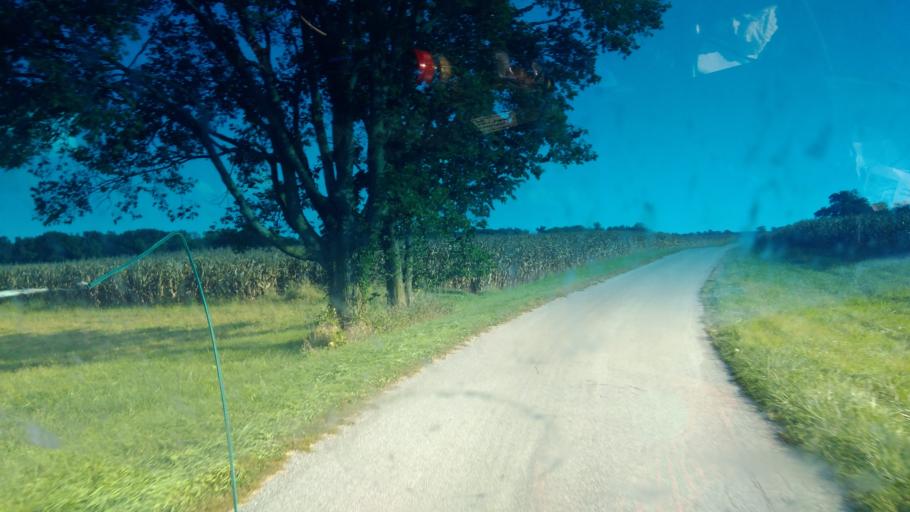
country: US
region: Ohio
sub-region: Wyandot County
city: Upper Sandusky
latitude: 40.8997
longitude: -83.2450
